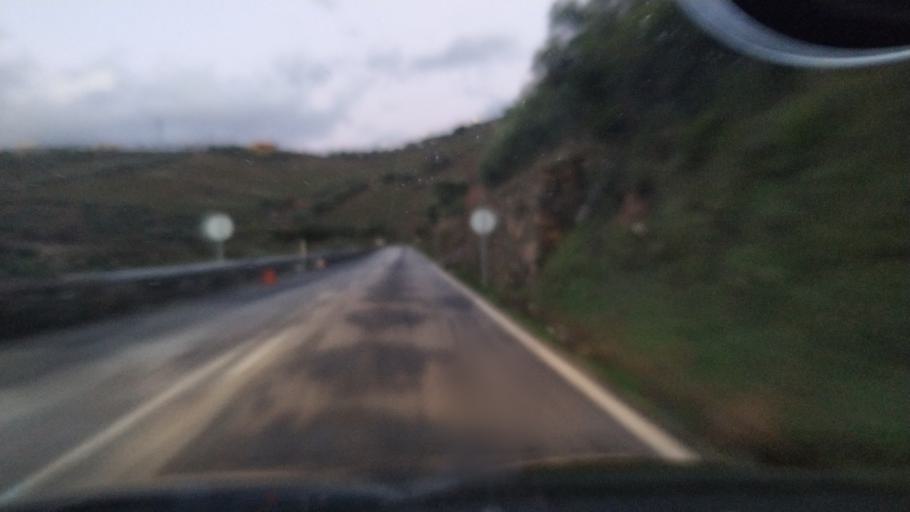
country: PT
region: Vila Real
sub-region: Santa Marta de Penaguiao
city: Santa Marta de Penaguiao
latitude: 41.2433
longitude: -7.7698
